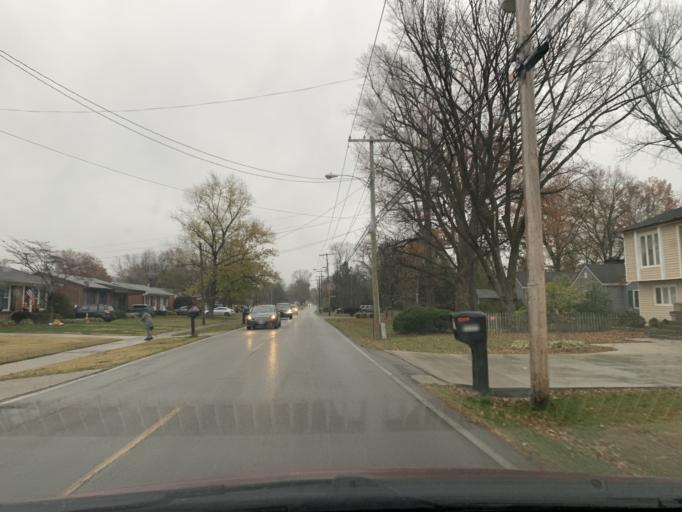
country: US
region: Kentucky
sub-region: Jefferson County
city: Buechel
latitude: 38.1982
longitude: -85.6391
